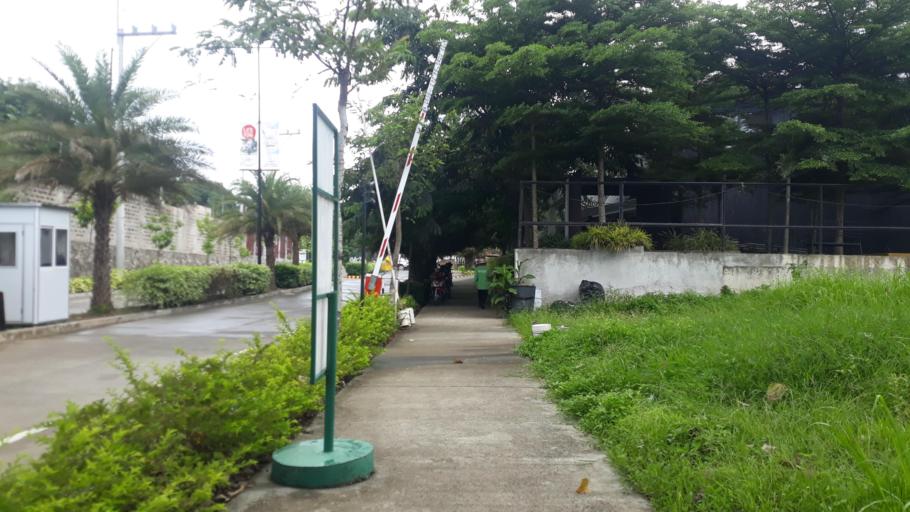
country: PH
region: Calabarzon
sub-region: Province of Cavite
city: Dasmarinas
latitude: 14.3001
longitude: 120.9498
